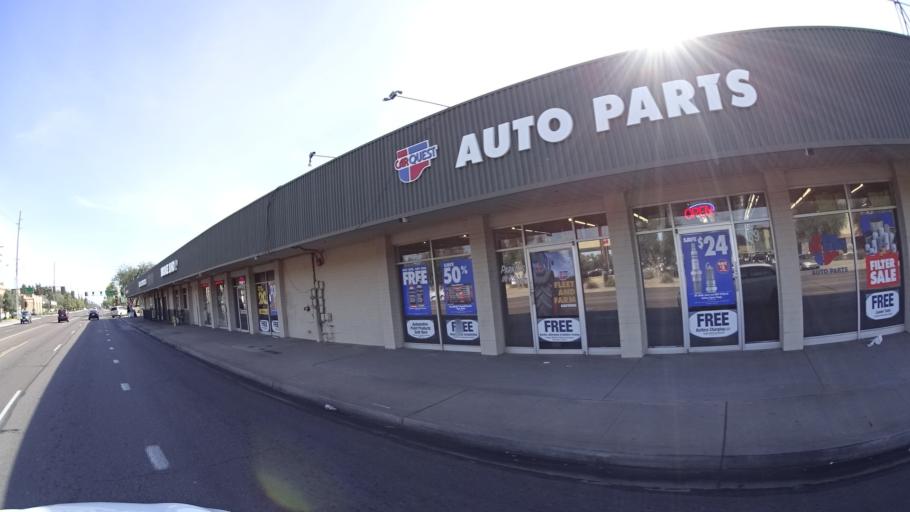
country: US
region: Arizona
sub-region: Maricopa County
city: Tempe Junction
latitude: 33.3928
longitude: -111.9410
